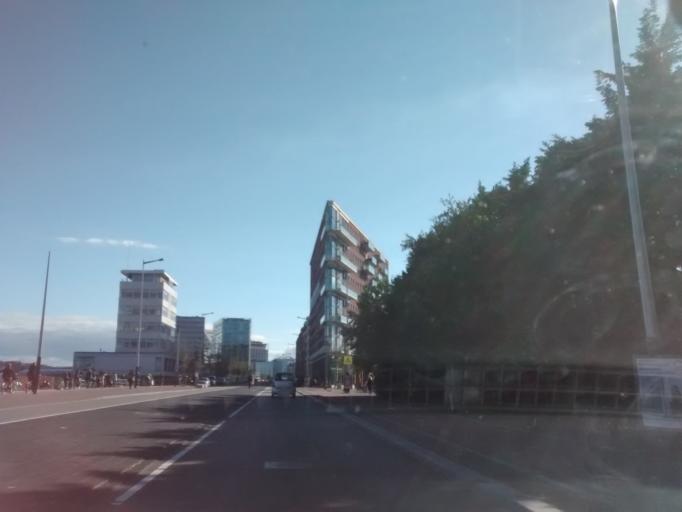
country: NL
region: North Holland
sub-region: Gemeente Amsterdam
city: Amsterdam
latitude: 52.3888
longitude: 4.8917
